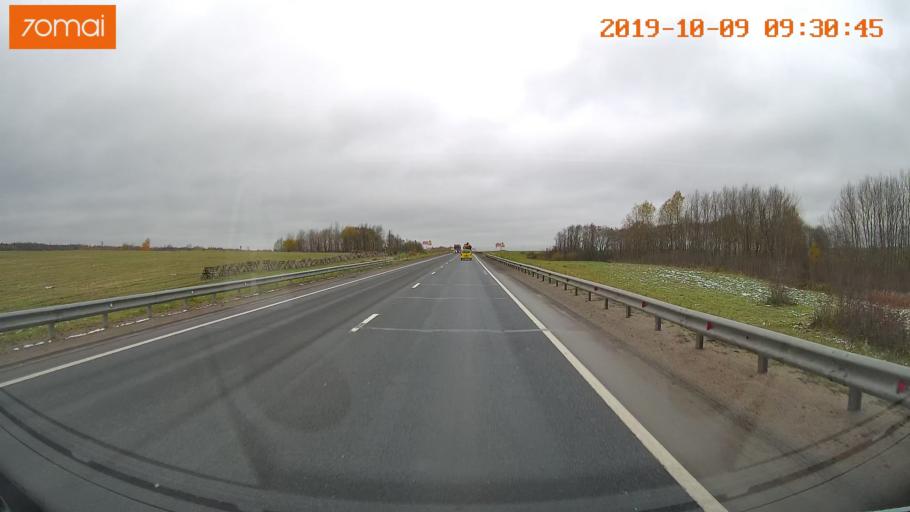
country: RU
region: Vologda
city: Vologda
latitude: 59.1429
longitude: 39.9461
